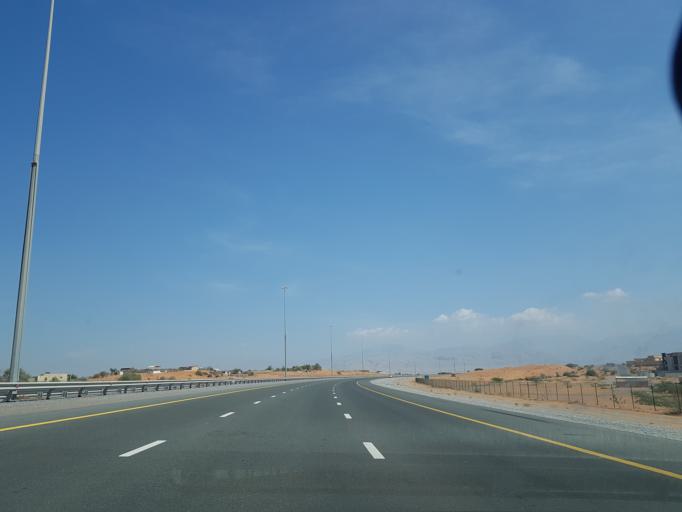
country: AE
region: Ra's al Khaymah
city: Ras al-Khaimah
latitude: 25.7040
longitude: 55.9377
